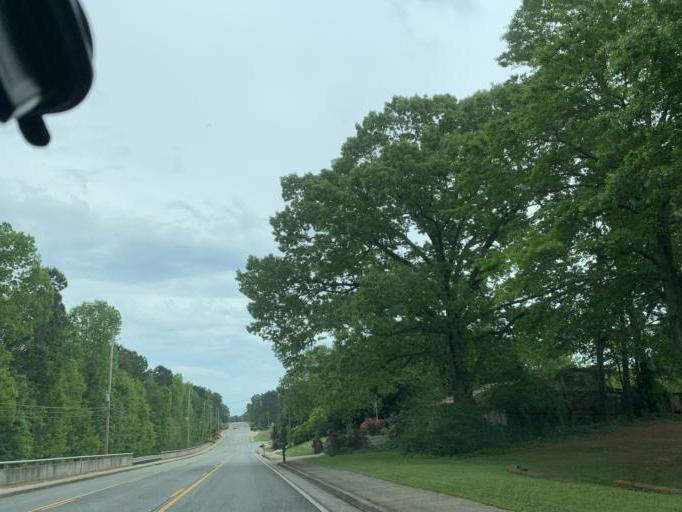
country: US
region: Georgia
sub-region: Forsyth County
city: Cumming
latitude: 34.1967
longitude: -84.1195
